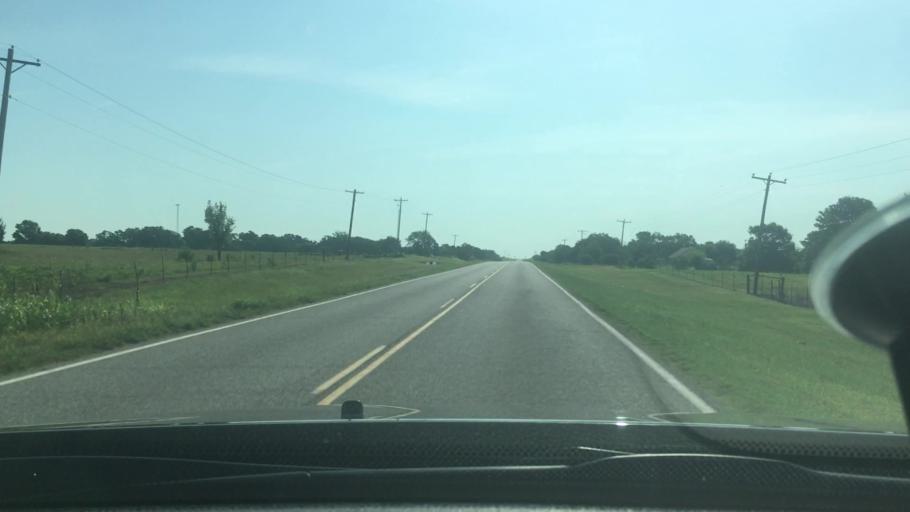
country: US
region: Oklahoma
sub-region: Garvin County
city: Wynnewood
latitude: 34.6518
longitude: -97.2581
